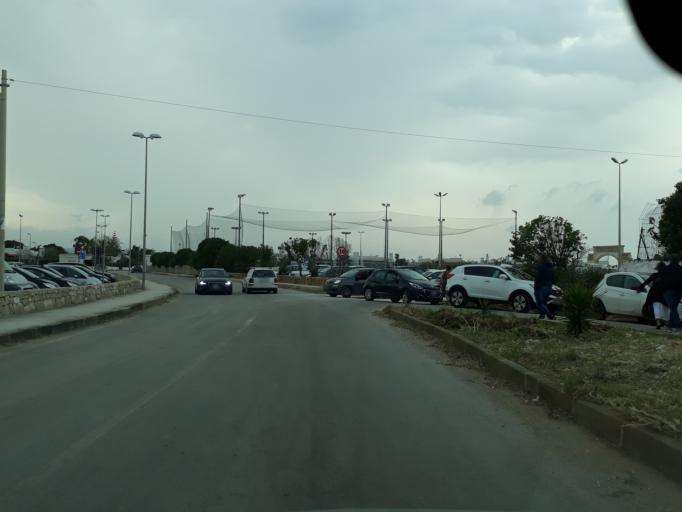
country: IT
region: Apulia
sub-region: Provincia di Brindisi
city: Ostuni
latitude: 40.7905
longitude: 17.5836
